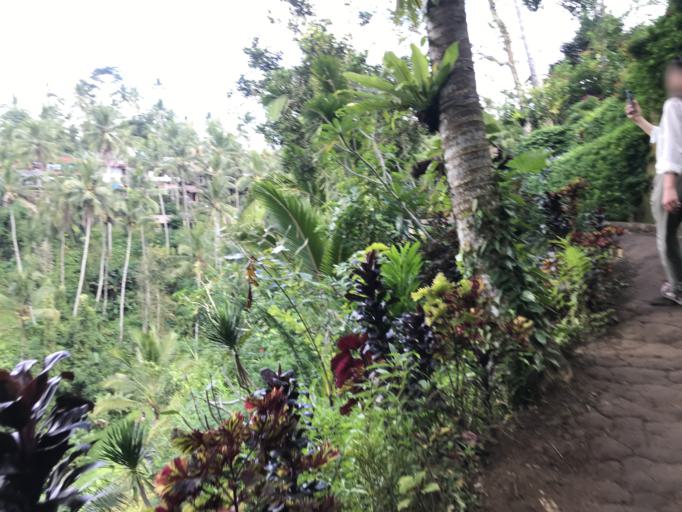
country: ID
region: Bali
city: Tegalalang
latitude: -8.4340
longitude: 115.2803
